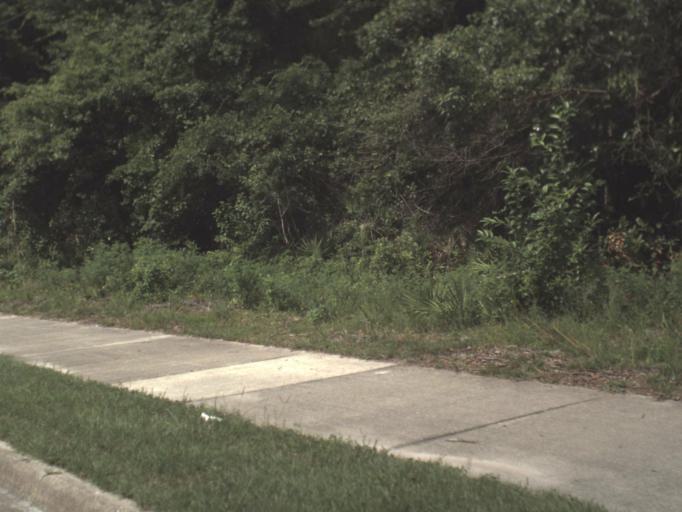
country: US
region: Florida
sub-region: Columbia County
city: Five Points
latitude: 30.2253
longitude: -82.6386
